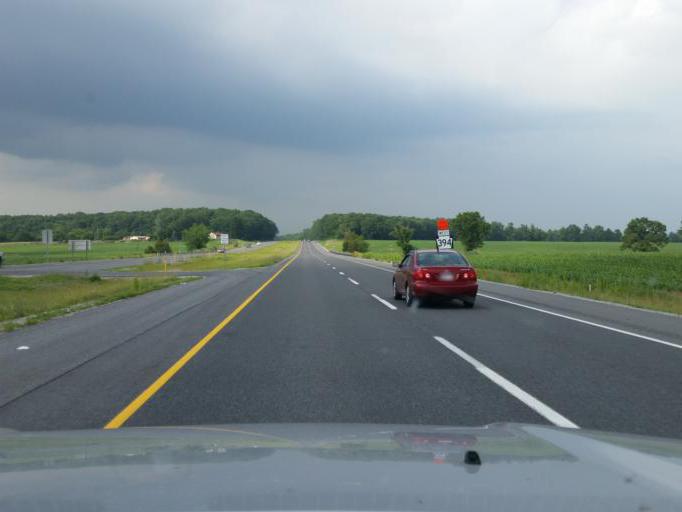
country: US
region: Pennsylvania
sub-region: Adams County
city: Biglerville
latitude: 39.8975
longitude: -77.1749
